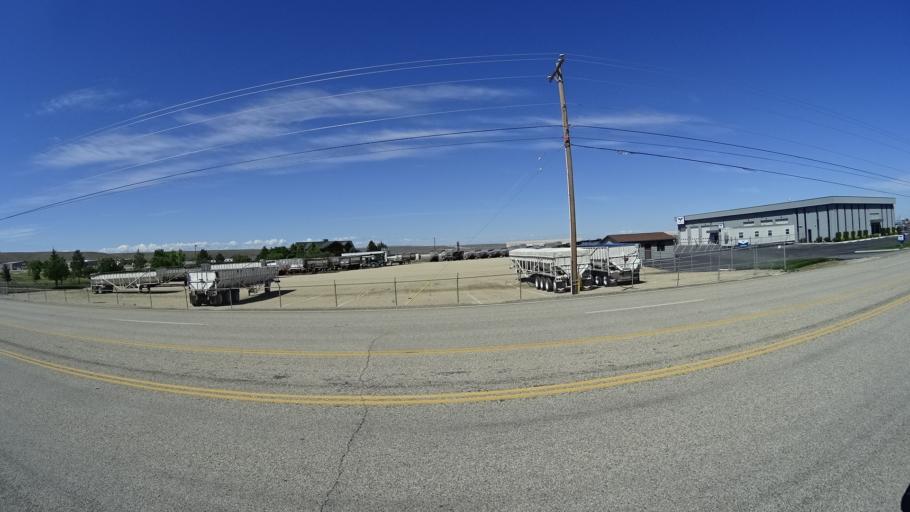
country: US
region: Idaho
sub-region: Ada County
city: Boise
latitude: 43.5320
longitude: -116.1517
